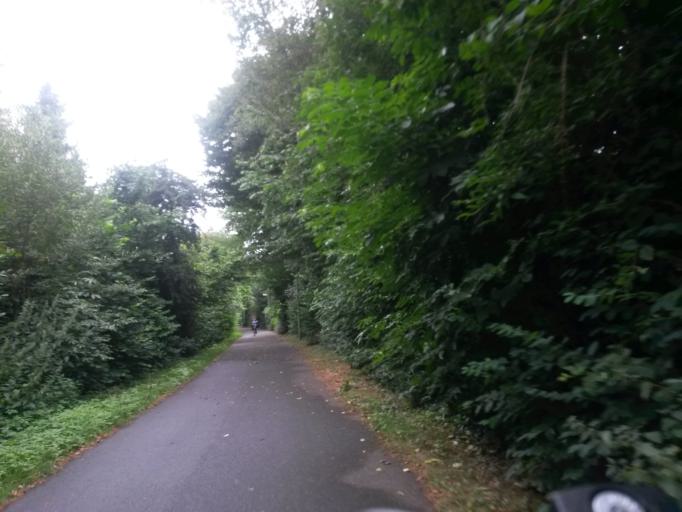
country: DE
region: North Rhine-Westphalia
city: Kempen
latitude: 51.3591
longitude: 6.4261
